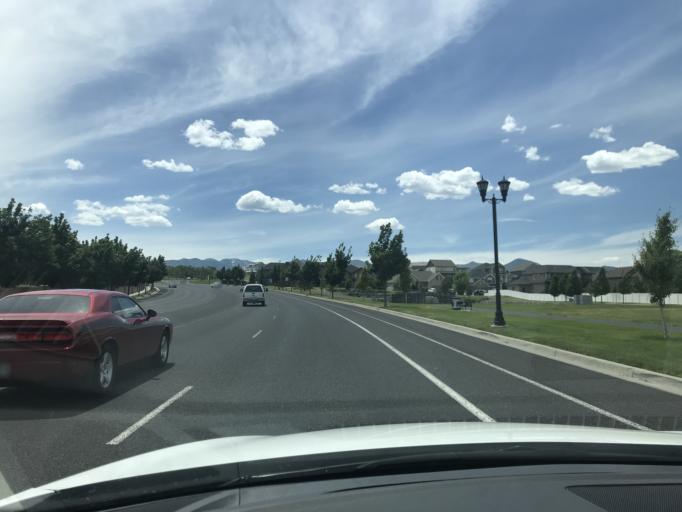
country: US
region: Utah
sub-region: Salt Lake County
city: South Jordan Heights
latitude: 40.5622
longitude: -111.9893
